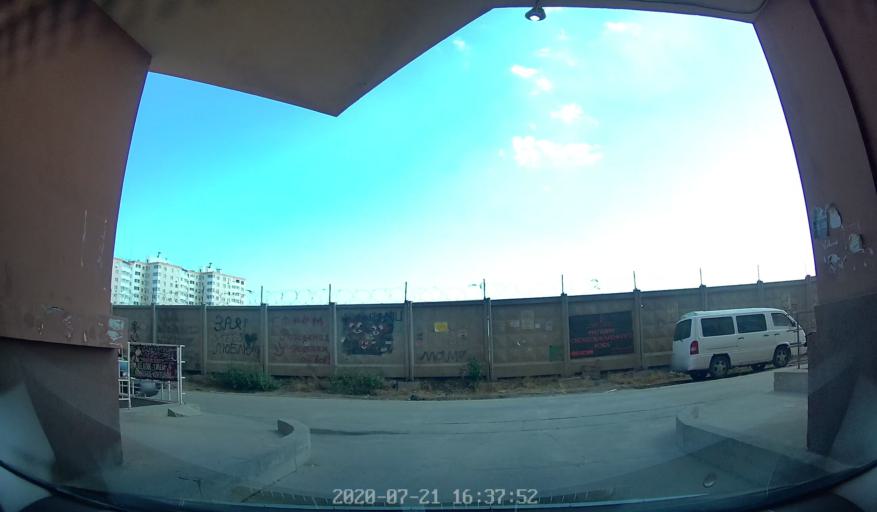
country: GR
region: South Aegean
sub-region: Nomos Kykladon
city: Serifos
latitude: 37.1205
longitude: 24.5641
